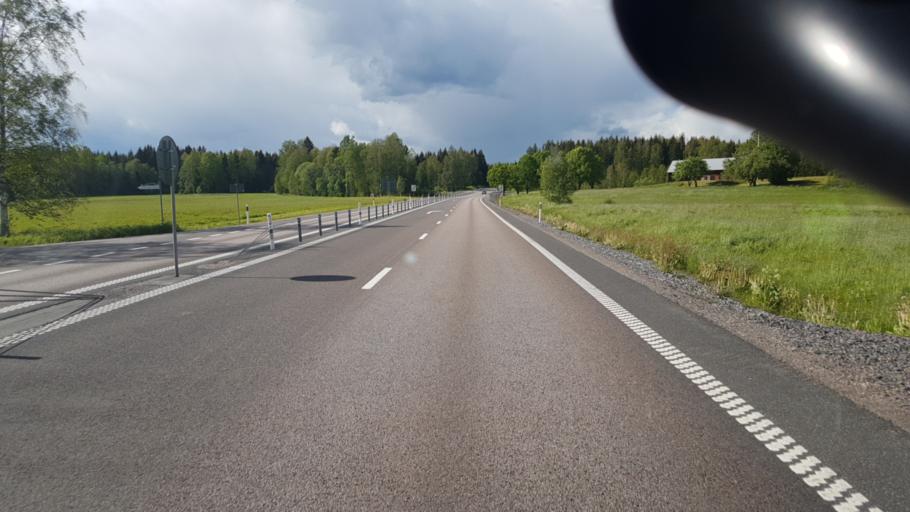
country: SE
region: Vaermland
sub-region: Eda Kommun
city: Amotfors
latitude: 59.7925
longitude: 12.3397
